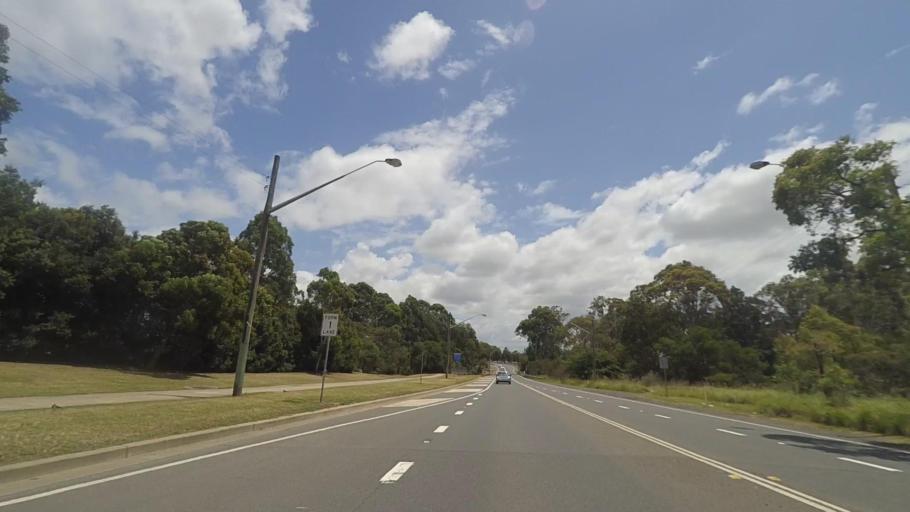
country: AU
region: New South Wales
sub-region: Liverpool
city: Holsworthy
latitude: -33.9597
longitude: 150.9586
